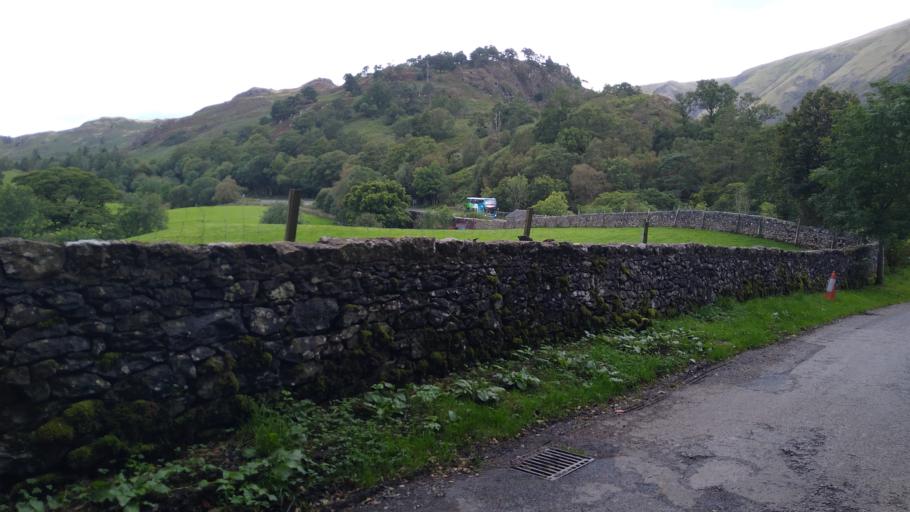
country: GB
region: England
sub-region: Cumbria
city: Keswick
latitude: 54.5652
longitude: -3.0605
